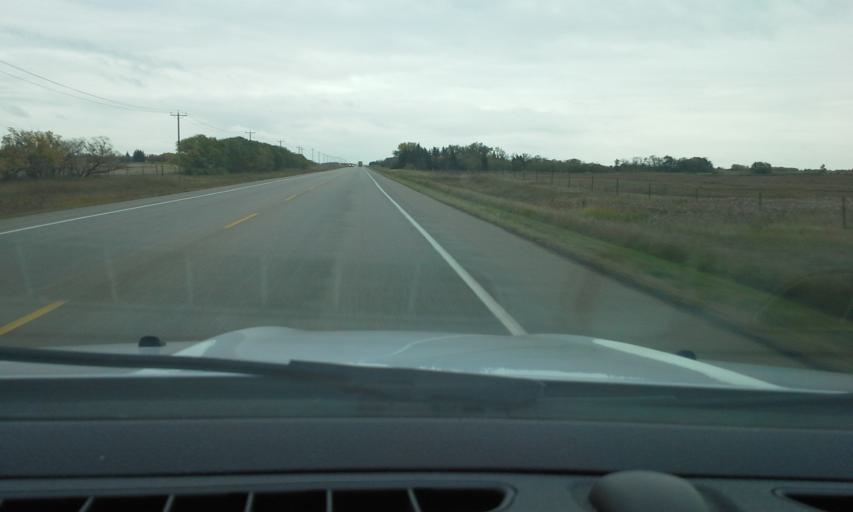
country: CA
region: Saskatchewan
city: Lloydminster
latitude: 53.2780
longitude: -109.8523
